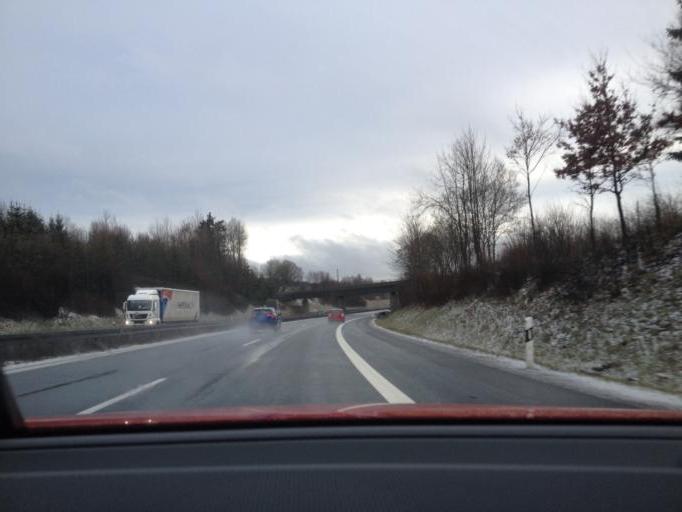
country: DE
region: Bavaria
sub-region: Upper Franconia
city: Schonwald
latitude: 50.1926
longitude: 12.1014
